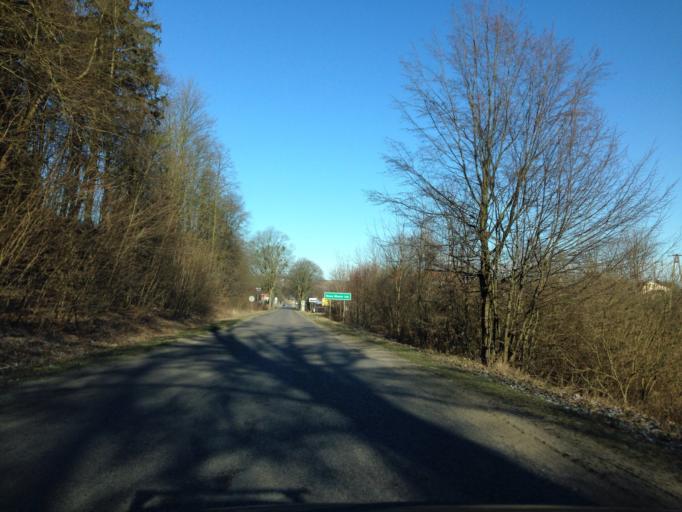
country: PL
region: Warmian-Masurian Voivodeship
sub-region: Powiat nowomiejski
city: Nowe Miasto Lubawskie
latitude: 53.4080
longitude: 19.6016
